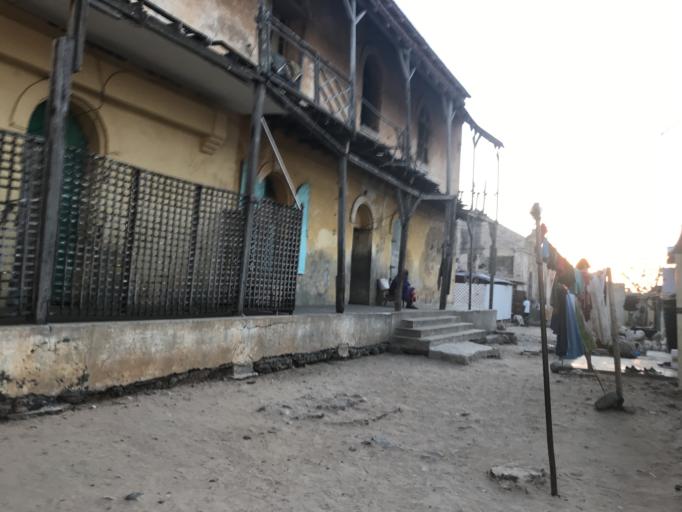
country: SN
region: Dakar
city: Dakar
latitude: 14.6672
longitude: -17.3993
